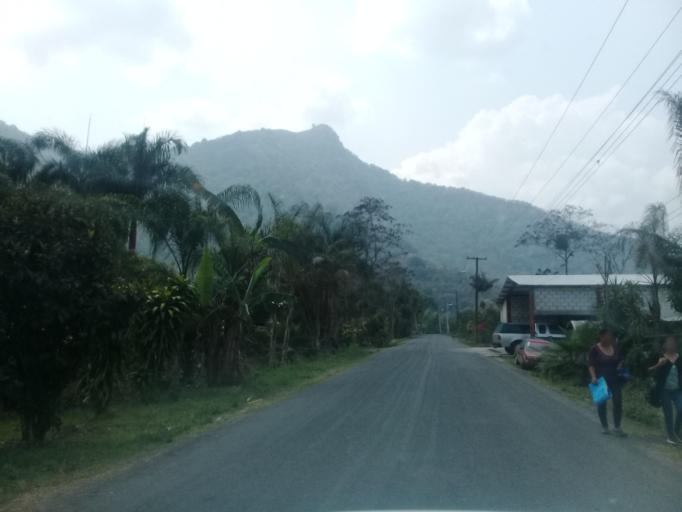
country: MX
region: Veracruz
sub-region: Ixtaczoquitlan
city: Capoluca
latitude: 18.8095
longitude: -96.9857
